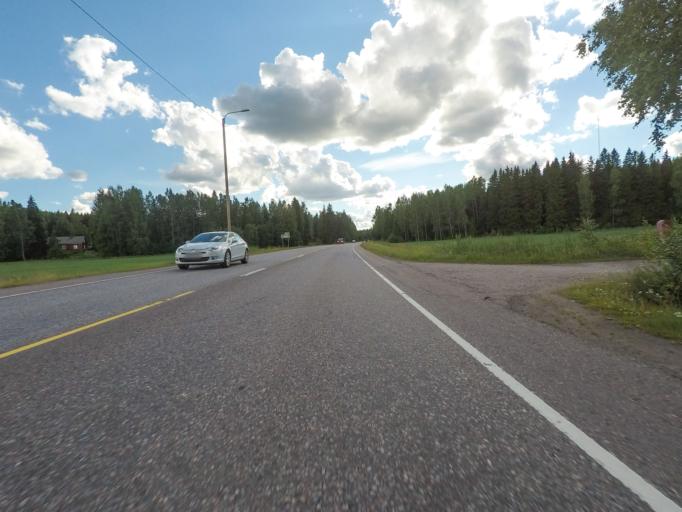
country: FI
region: Uusimaa
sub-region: Helsinki
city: Vihti
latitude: 60.4455
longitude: 24.5093
